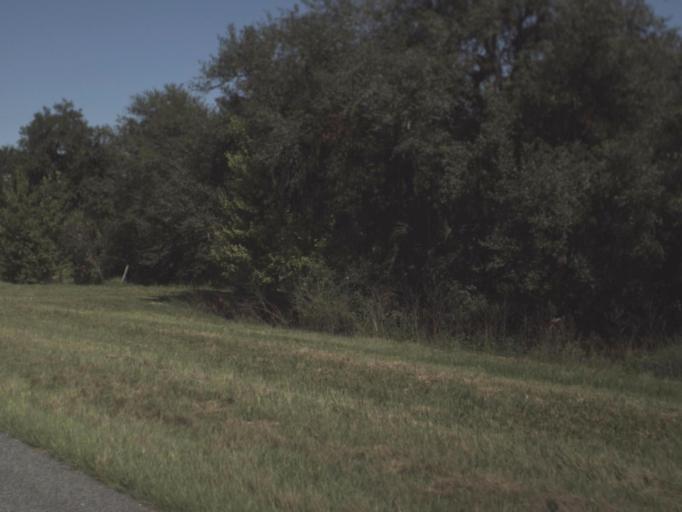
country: US
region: Florida
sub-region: Hendry County
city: Port LaBelle
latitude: 26.9541
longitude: -81.3164
